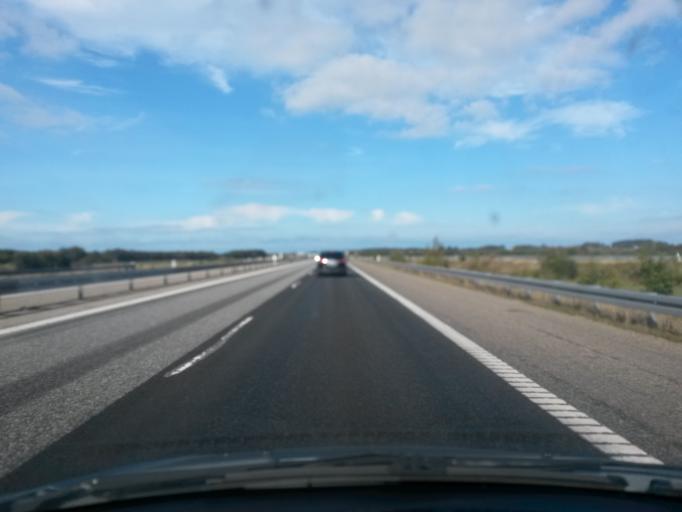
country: DK
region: Central Jutland
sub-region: Herning Kommune
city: Gjellerup Kirkeby
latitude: 56.1354
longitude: 9.0127
